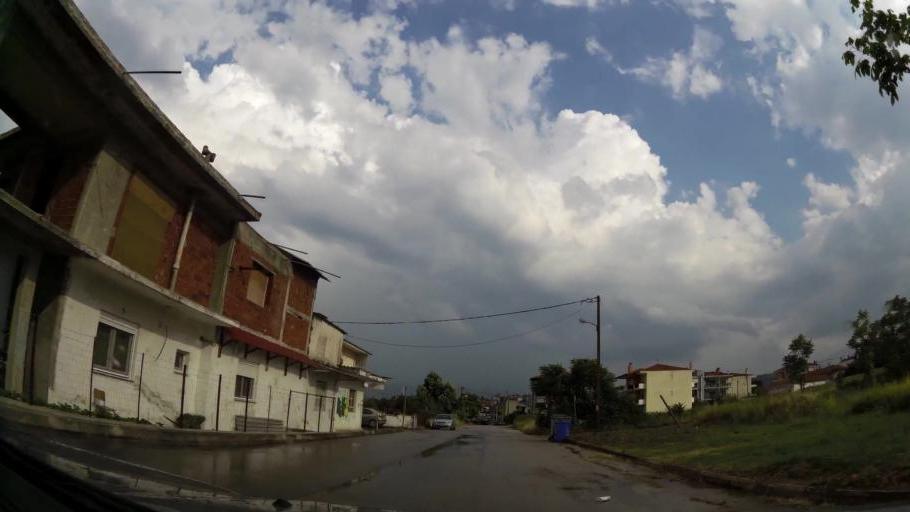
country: GR
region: Central Macedonia
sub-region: Nomos Imathias
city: Veroia
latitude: 40.5397
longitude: 22.2005
